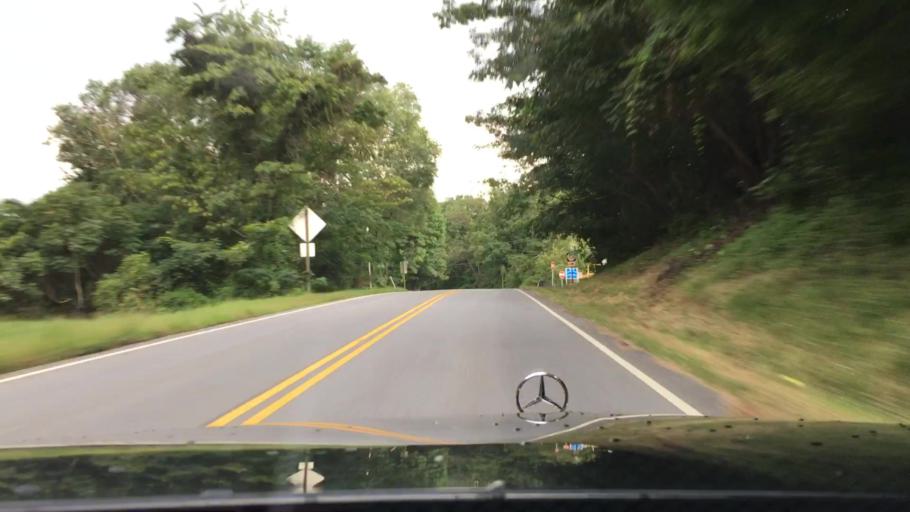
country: US
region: Virginia
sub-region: Nelson County
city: Lovingston
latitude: 37.7950
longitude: -78.9721
